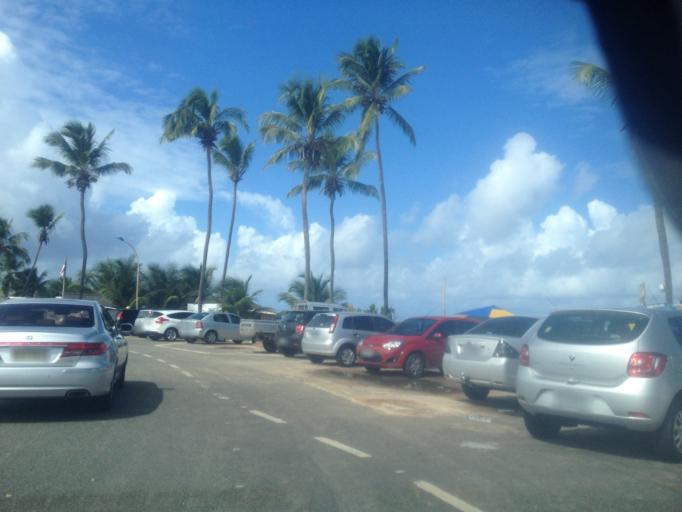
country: BR
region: Bahia
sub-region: Camacari
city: Camacari
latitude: -12.6520
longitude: -38.0688
